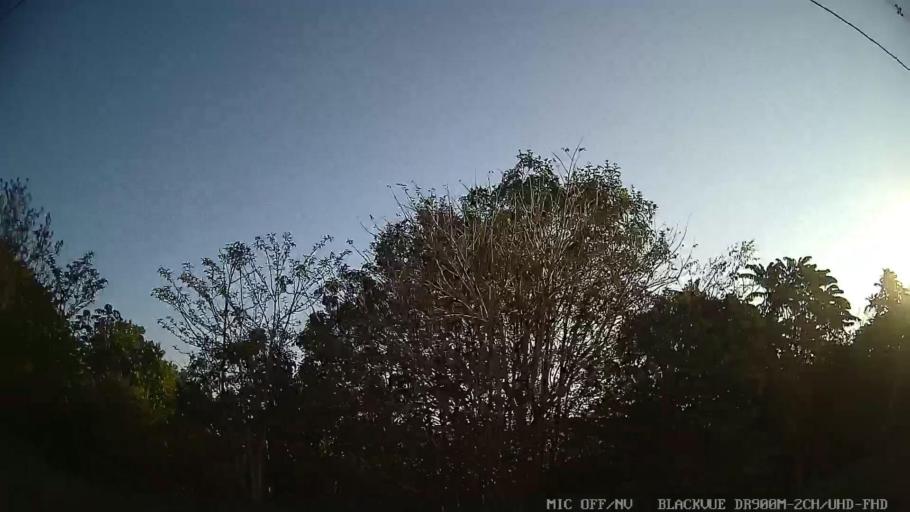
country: BR
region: Sao Paulo
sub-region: Itupeva
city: Itupeva
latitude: -23.2462
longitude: -47.0516
